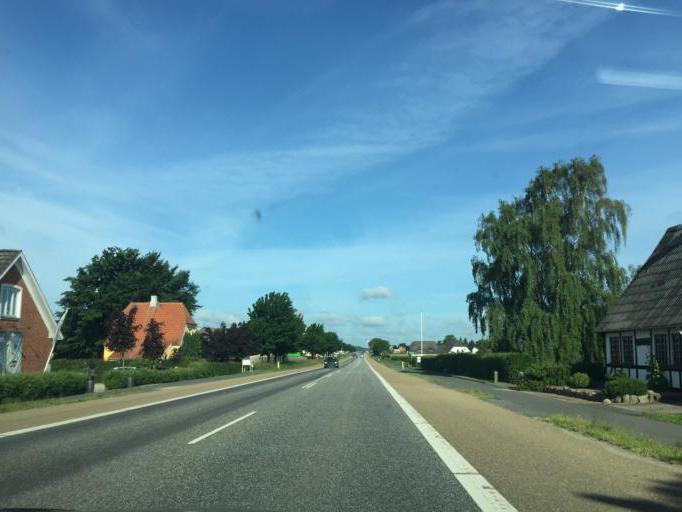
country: DK
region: South Denmark
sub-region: Middelfart Kommune
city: Strib
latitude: 55.4937
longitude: 9.7832
